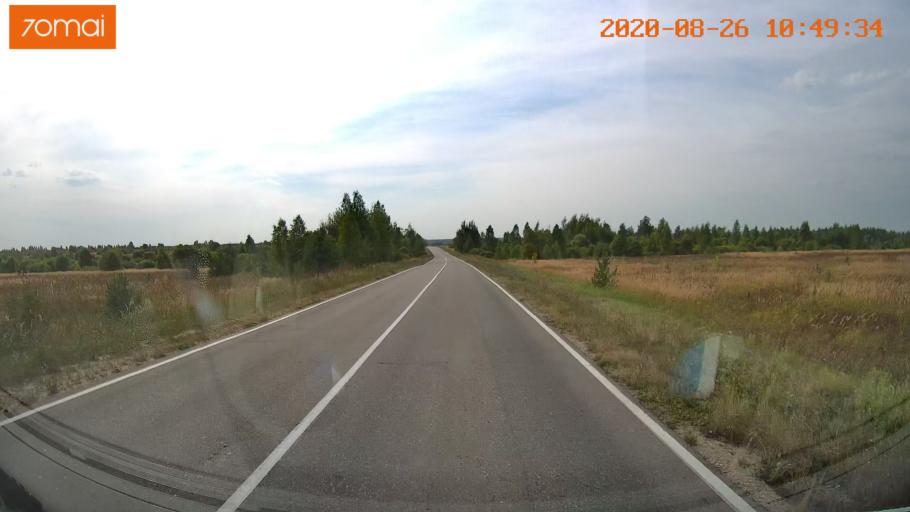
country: RU
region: Rjazan
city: Lashma
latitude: 54.7005
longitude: 41.1590
